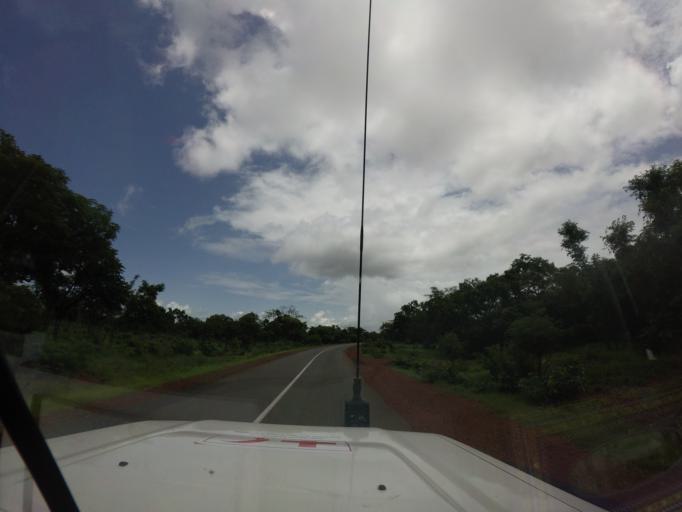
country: GN
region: Faranah
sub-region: Faranah Prefecture
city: Faranah
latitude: 10.0205
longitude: -10.8182
